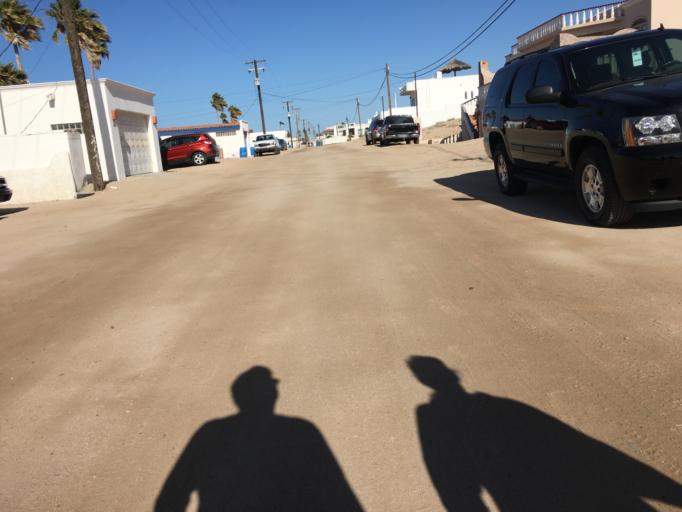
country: MX
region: Sonora
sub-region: Puerto Penasco
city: Puerto Penasco
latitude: 31.2903
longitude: -113.4971
